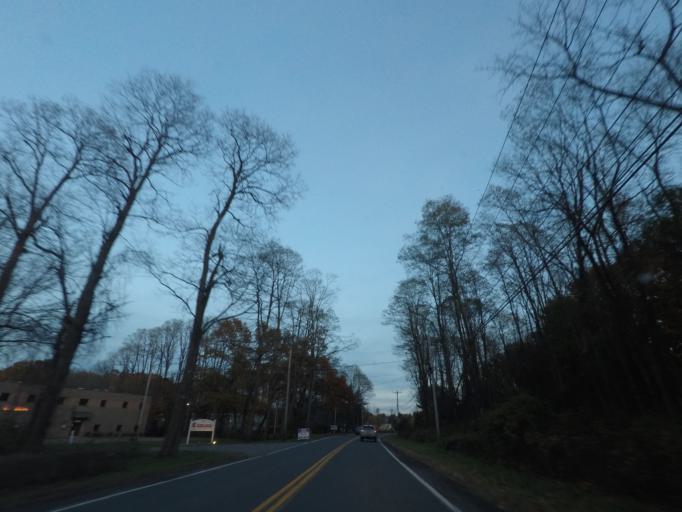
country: US
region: New York
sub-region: Schenectady County
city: Rotterdam
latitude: 42.7480
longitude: -73.9117
